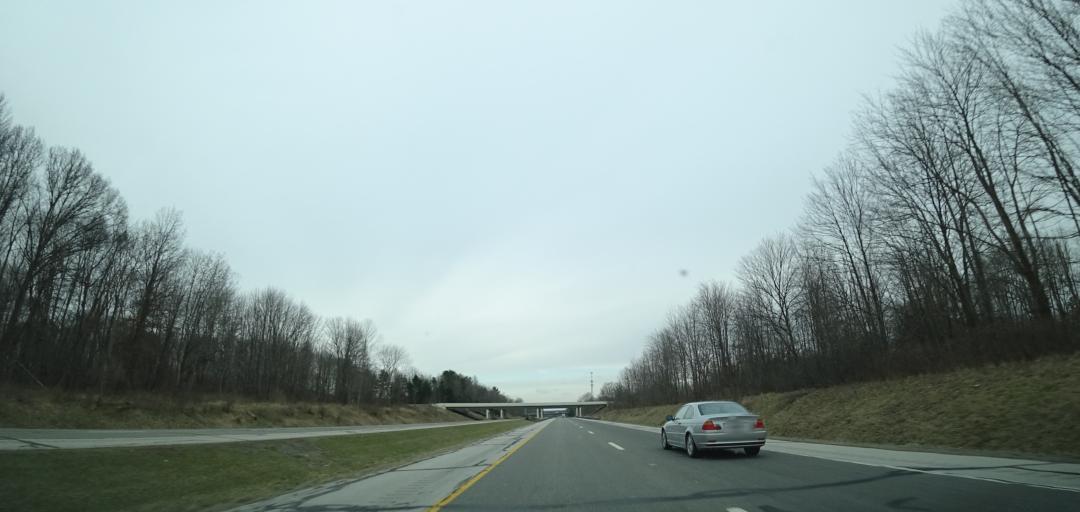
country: US
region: Ohio
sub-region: Mahoning County
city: Canfield
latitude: 41.0341
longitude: -80.7433
